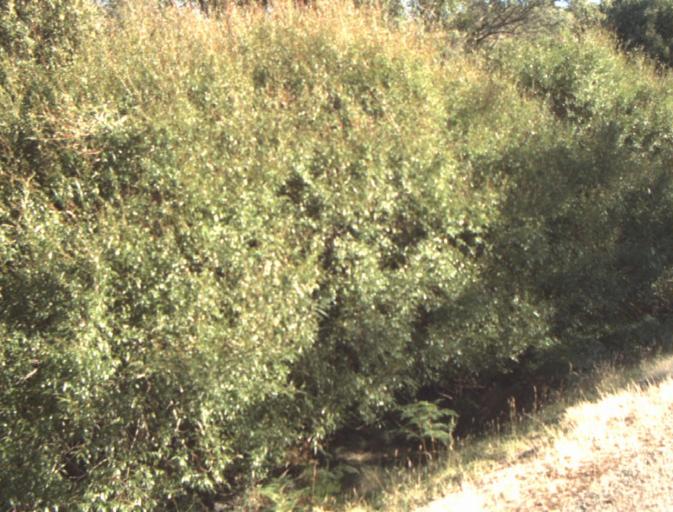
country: AU
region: Tasmania
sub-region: Launceston
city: Newstead
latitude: -41.4205
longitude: 147.2568
